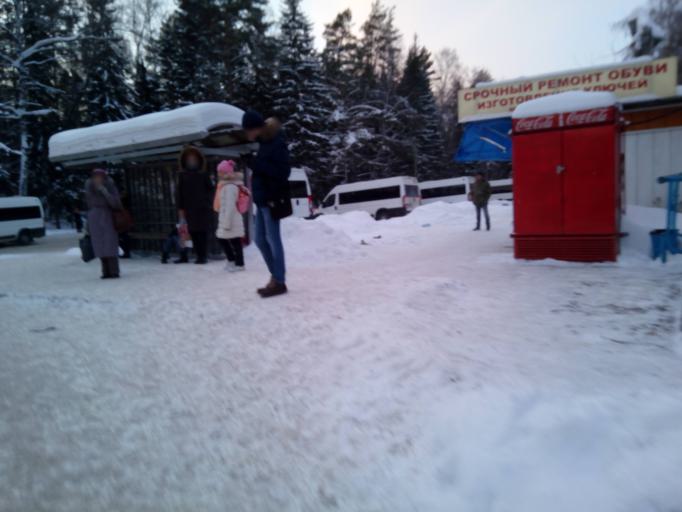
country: RU
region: Novosibirsk
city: Akademgorodok
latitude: 54.8397
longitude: 83.0875
